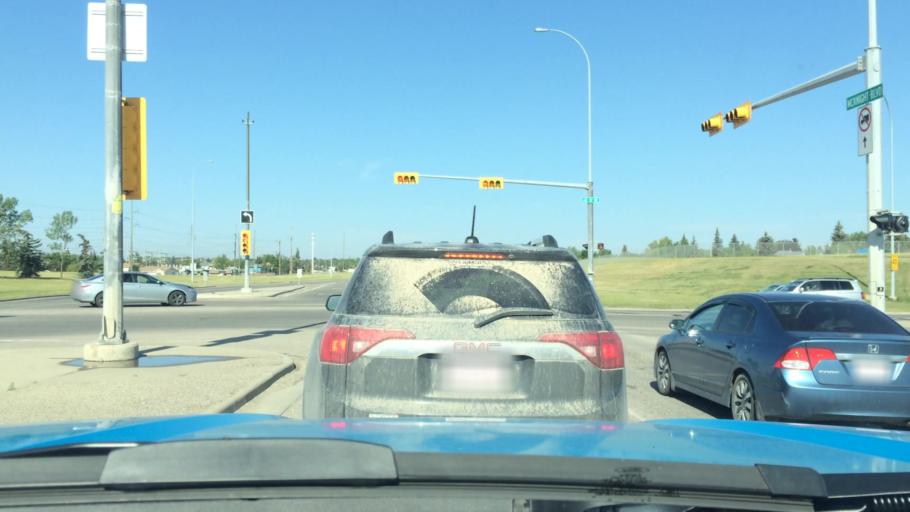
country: CA
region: Alberta
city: Chestermere
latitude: 51.0962
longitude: -113.9347
